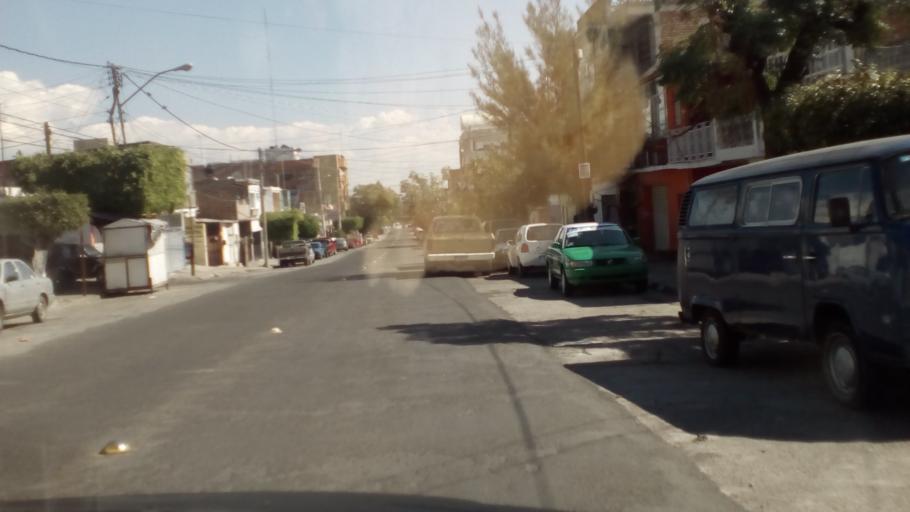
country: MX
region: Guanajuato
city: Leon
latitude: 21.1203
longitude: -101.6935
